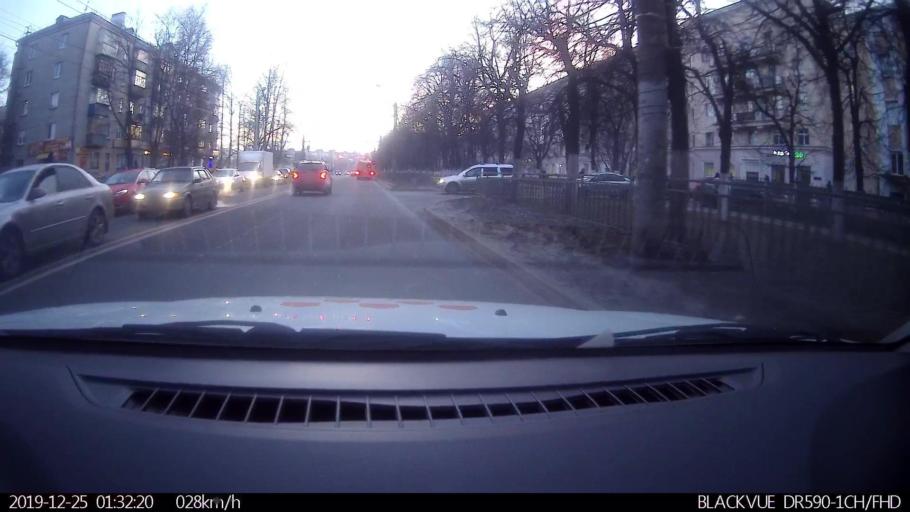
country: RU
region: Nizjnij Novgorod
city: Gorbatovka
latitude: 56.2443
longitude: 43.8640
